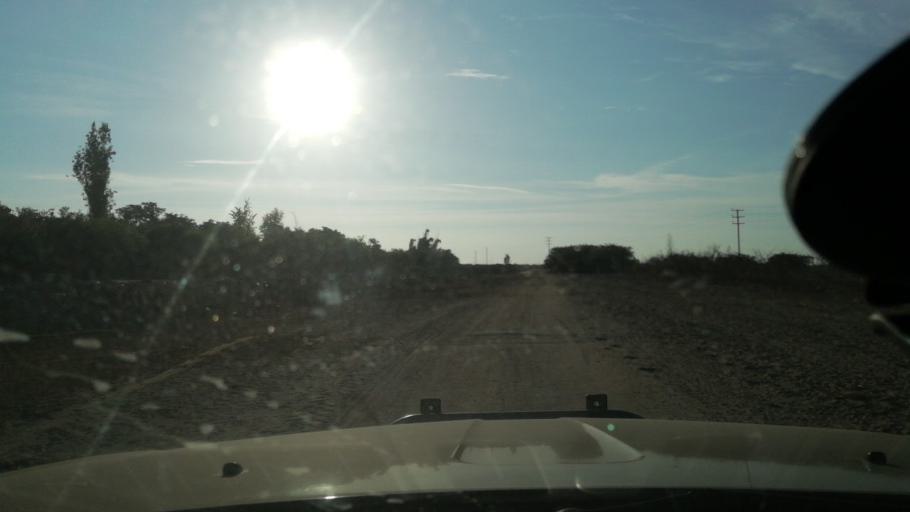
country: PE
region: Ica
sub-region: Provincia de Chincha
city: San Pedro
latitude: -13.3385
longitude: -76.1647
